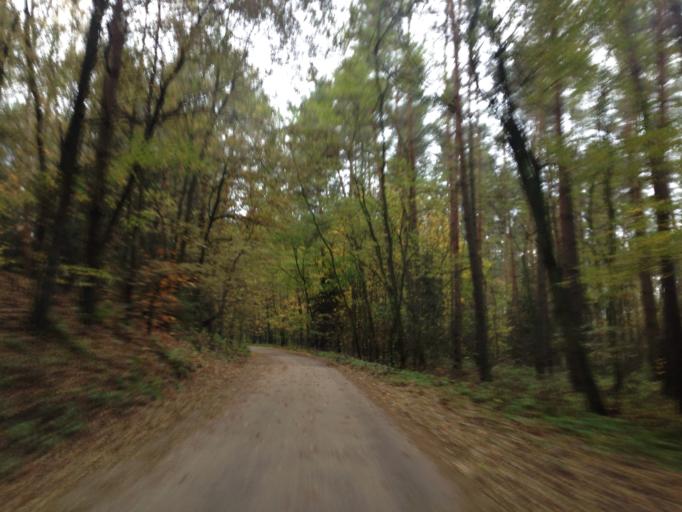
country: PL
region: Kujawsko-Pomorskie
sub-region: Powiat brodnicki
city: Brzozie
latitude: 53.3062
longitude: 19.5589
